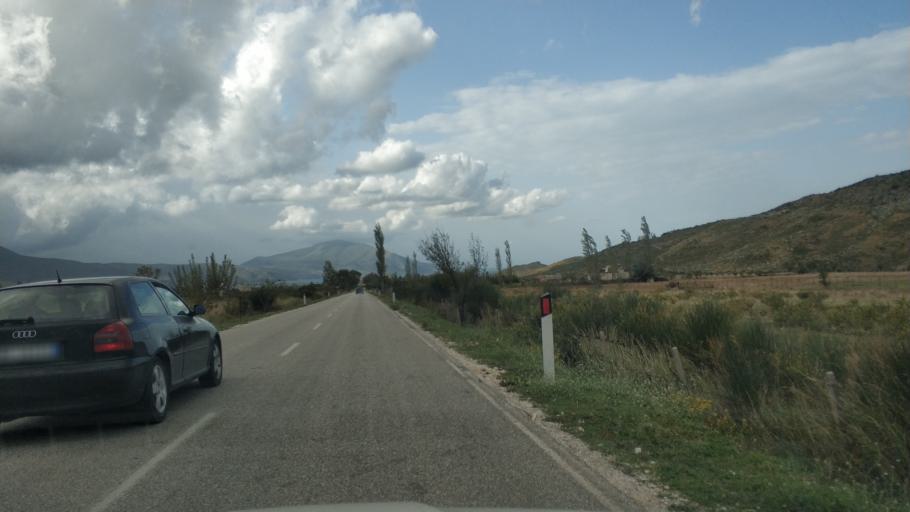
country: AL
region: Vlore
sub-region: Rrethi i Vlores
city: Orikum
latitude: 40.2741
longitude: 19.5095
